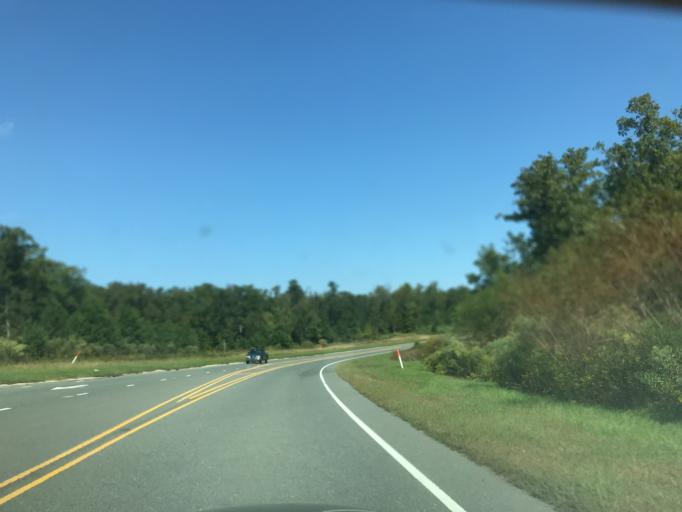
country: US
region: North Carolina
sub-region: Wake County
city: Morrisville
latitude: 35.8680
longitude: -78.8848
